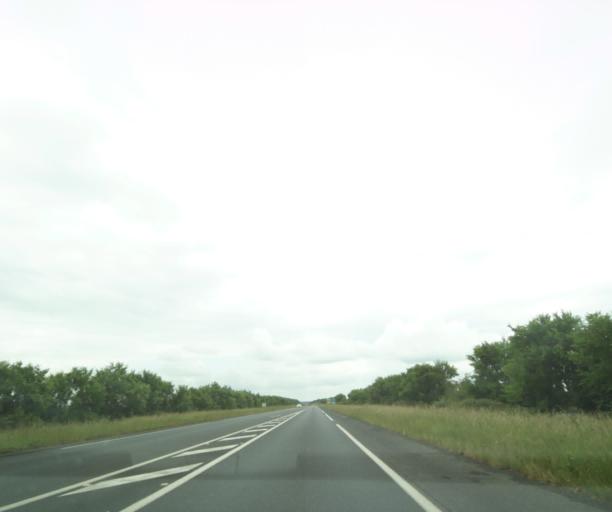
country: FR
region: Poitou-Charentes
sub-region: Departement des Deux-Sevres
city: Saint-Varent
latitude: 46.8781
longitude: -0.1964
